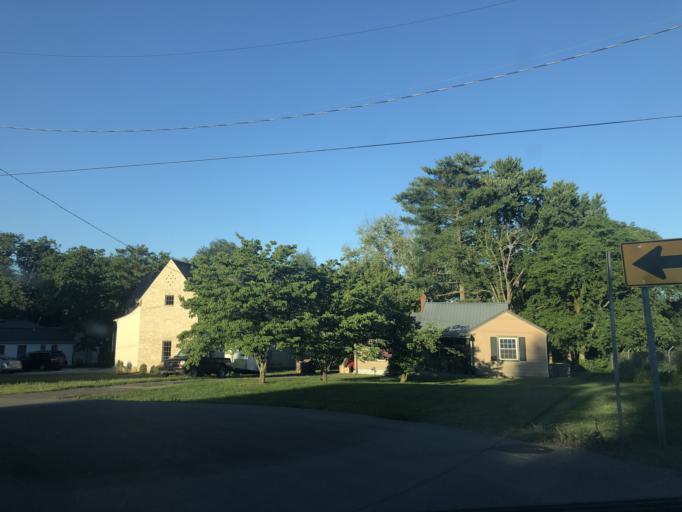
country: US
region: Tennessee
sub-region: Davidson County
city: Oak Hill
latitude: 36.0902
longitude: -86.7840
